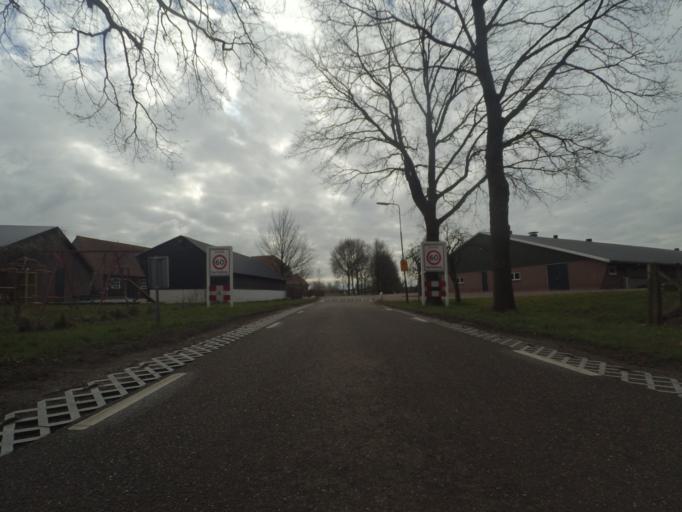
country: NL
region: Utrecht
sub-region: Gemeente Utrechtse Heuvelrug
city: Overberg
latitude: 52.0547
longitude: 5.4809
